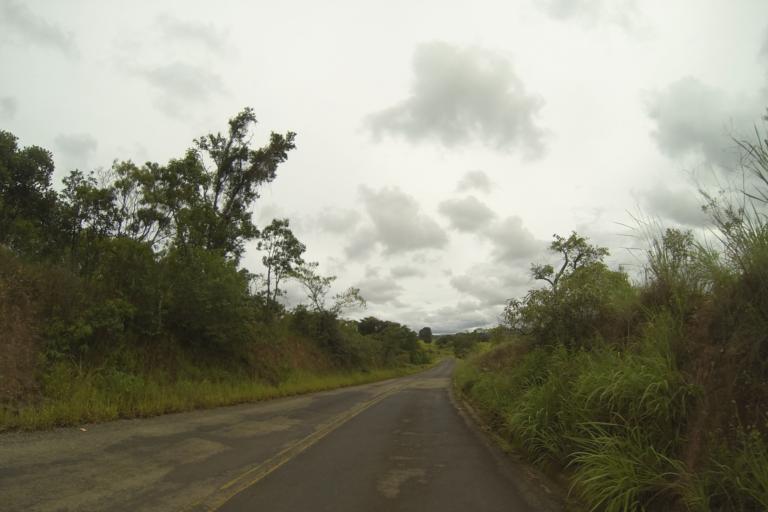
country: BR
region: Minas Gerais
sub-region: Ibia
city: Ibia
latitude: -19.6963
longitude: -46.4354
